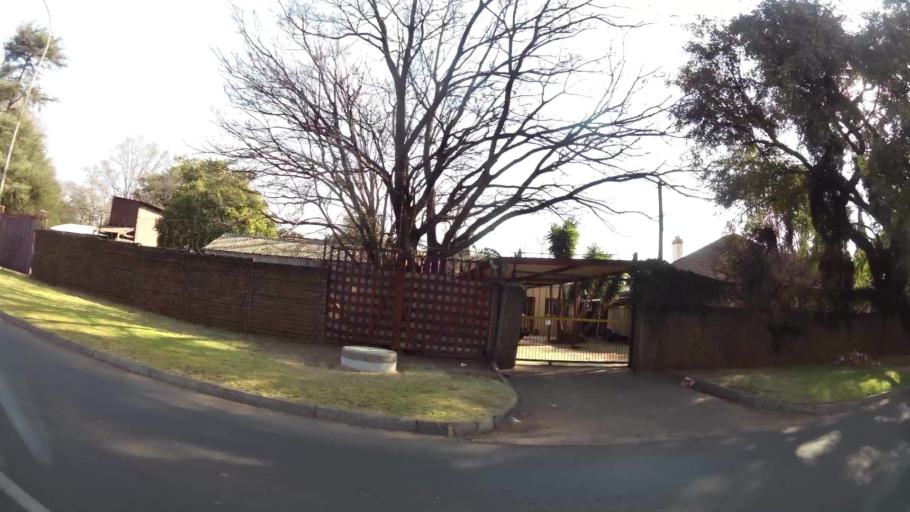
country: ZA
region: Gauteng
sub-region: Ekurhuleni Metropolitan Municipality
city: Tembisa
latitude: -25.9537
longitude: 28.2294
